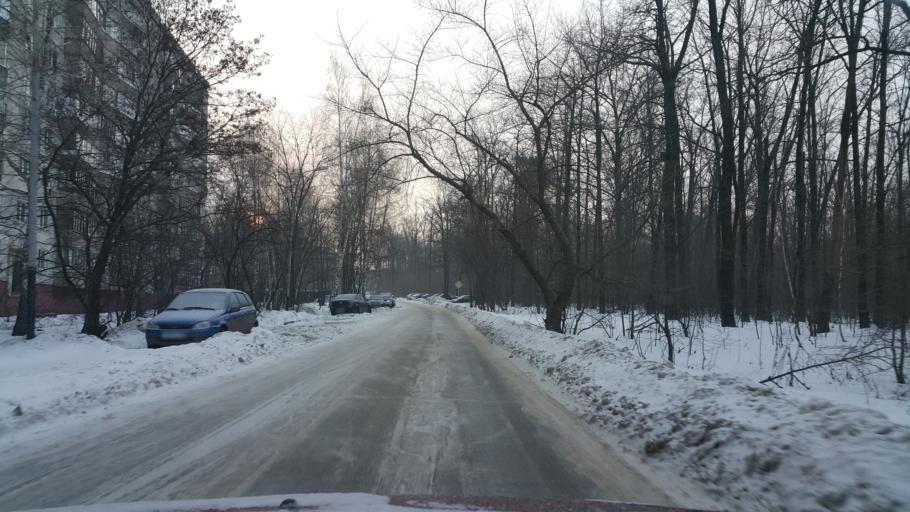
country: RU
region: Tambov
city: Kotovsk
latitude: 52.5749
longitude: 41.5174
